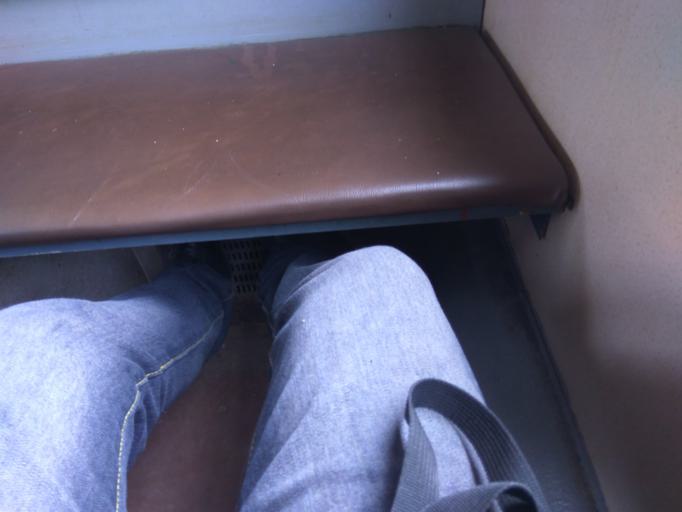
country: RU
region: Moskovskaya
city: Beloozerskiy
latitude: 55.4726
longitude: 38.4260
